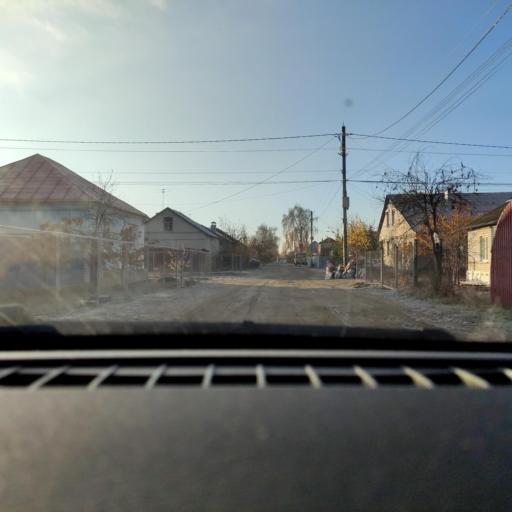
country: RU
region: Voronezj
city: Somovo
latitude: 51.7415
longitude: 39.2771
